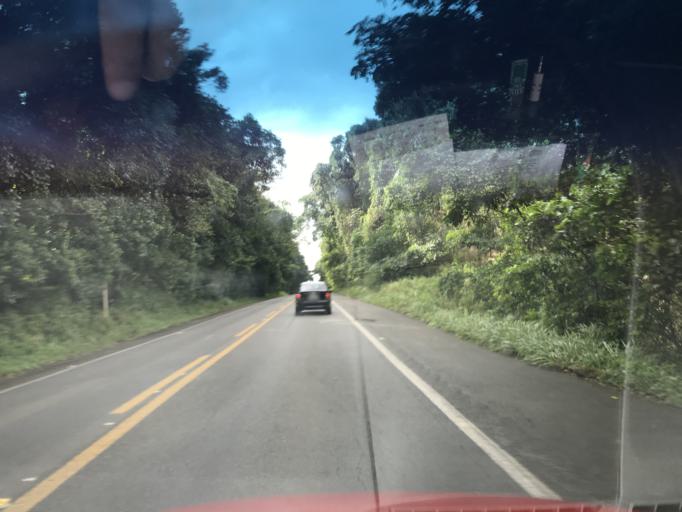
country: BR
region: Bahia
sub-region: Itajuipe
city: Itajuipe
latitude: -14.6320
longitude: -39.3344
